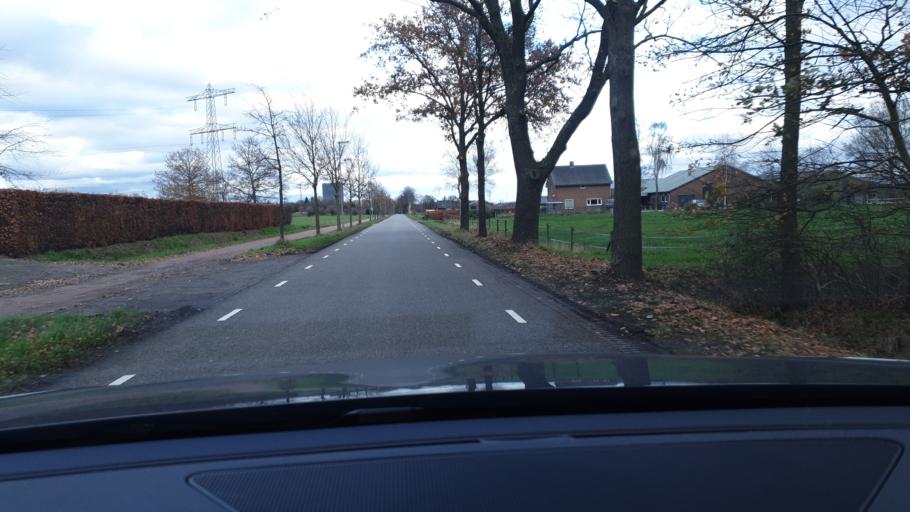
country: NL
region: North Brabant
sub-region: Gemeente Veldhoven
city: Veldhoven
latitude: 51.3891
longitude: 5.4091
